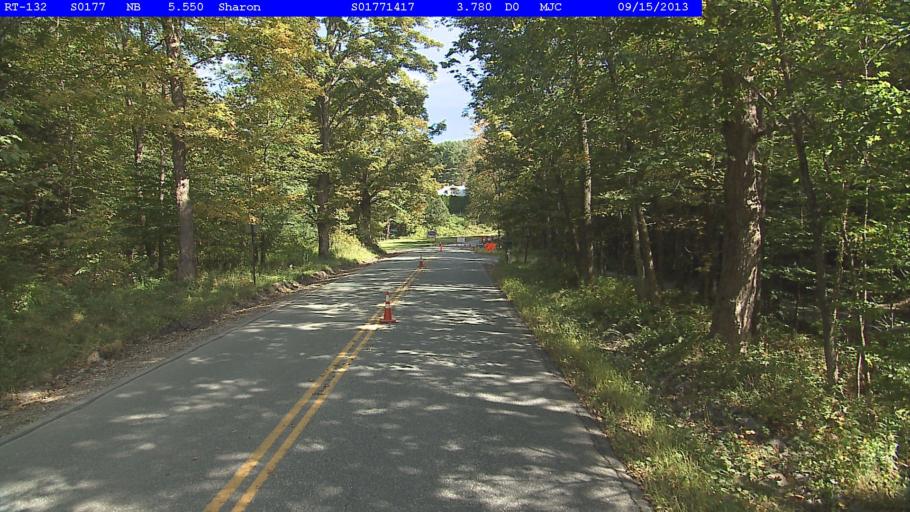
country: US
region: New Hampshire
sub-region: Grafton County
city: Hanover
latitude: 43.7930
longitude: -72.4474
